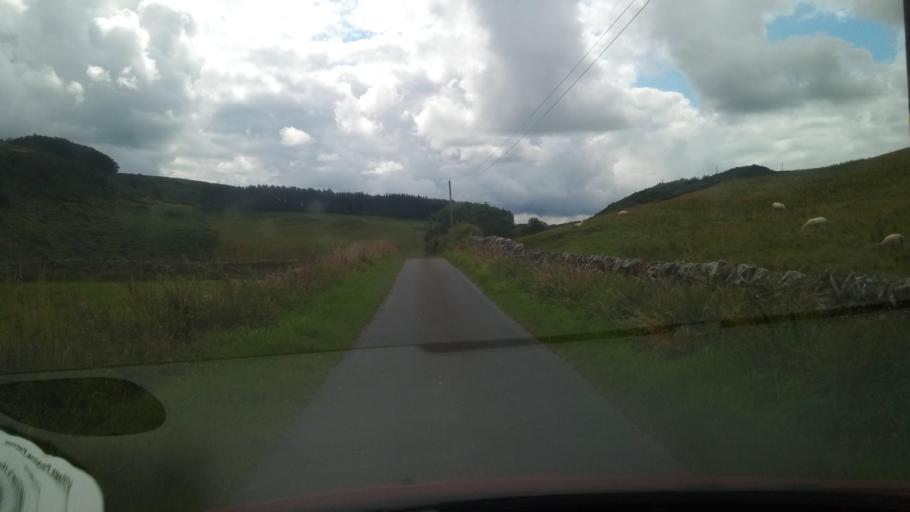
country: GB
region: Scotland
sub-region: The Scottish Borders
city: Hawick
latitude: 55.4150
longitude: -2.7573
